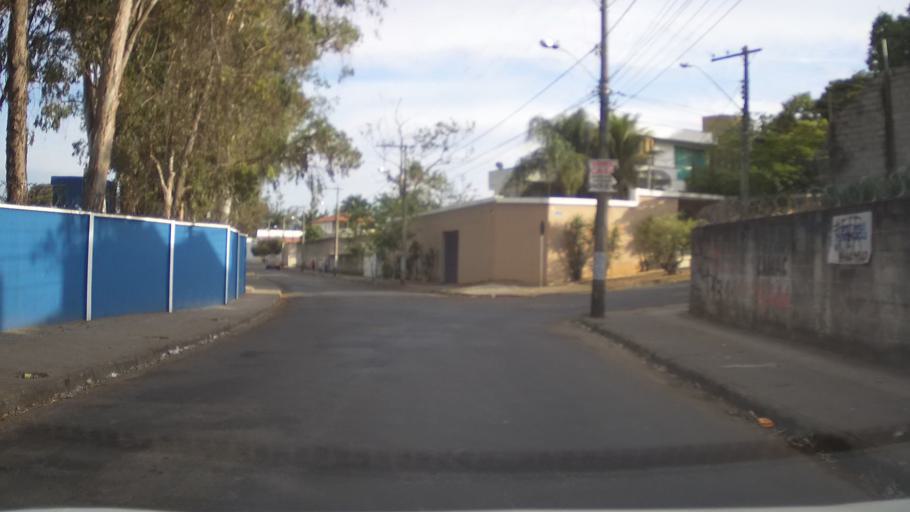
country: BR
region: Minas Gerais
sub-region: Belo Horizonte
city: Belo Horizonte
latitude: -19.8647
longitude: -43.9959
